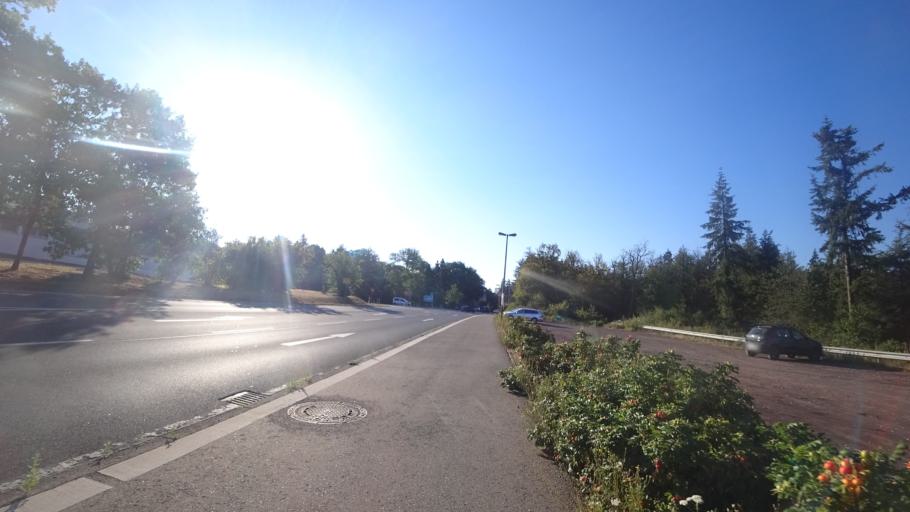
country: DE
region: Rheinland-Pfalz
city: Kratzenburg
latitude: 50.2128
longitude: 7.5486
